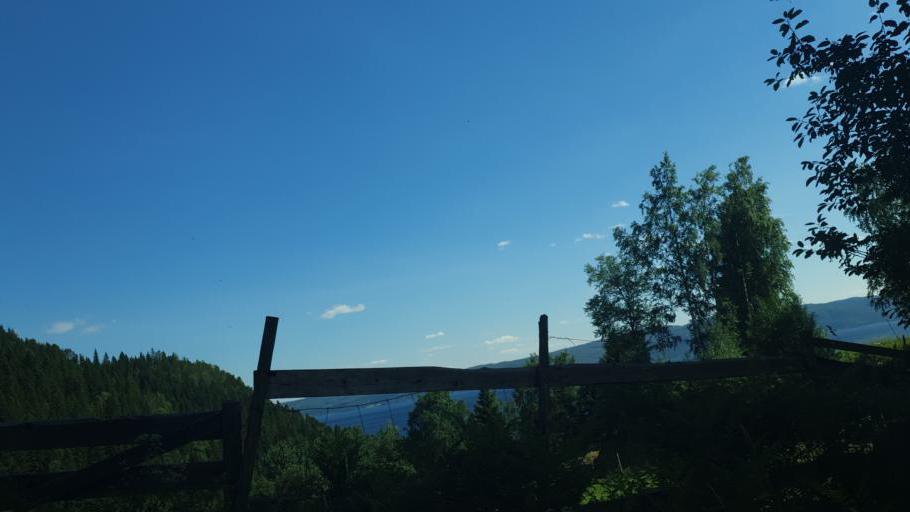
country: NO
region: Nord-Trondelag
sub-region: Frosta
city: Frosta
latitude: 63.7101
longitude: 10.7756
